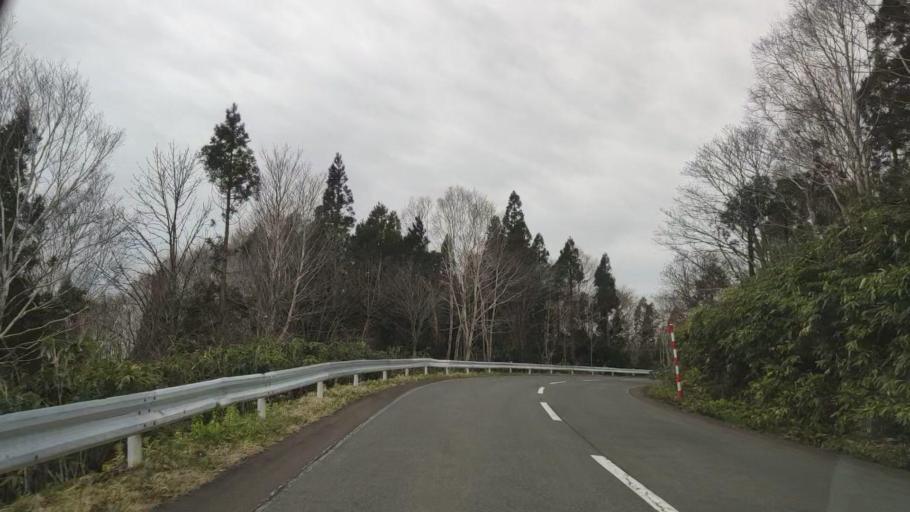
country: JP
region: Akita
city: Hanawa
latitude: 40.4158
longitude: 140.8432
